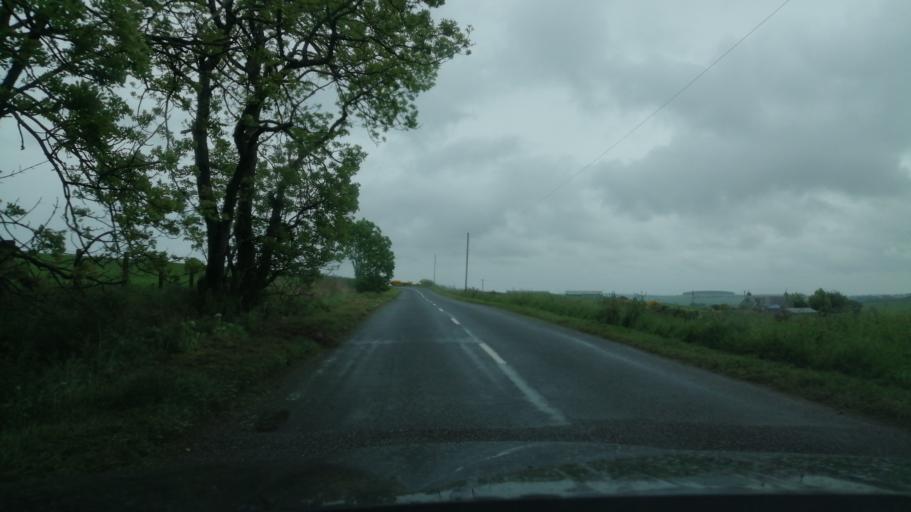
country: GB
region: Scotland
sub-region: Aberdeenshire
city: Portsoy
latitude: 57.6037
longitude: -2.7275
